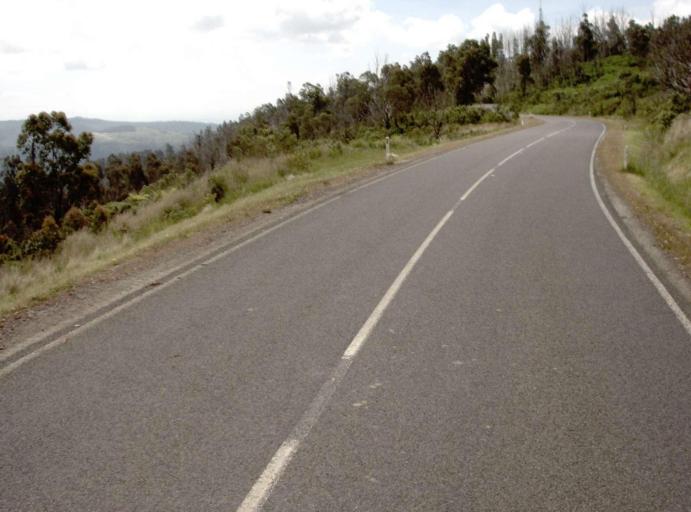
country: AU
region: Victoria
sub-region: Latrobe
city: Traralgon
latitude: -38.4030
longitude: 146.5633
